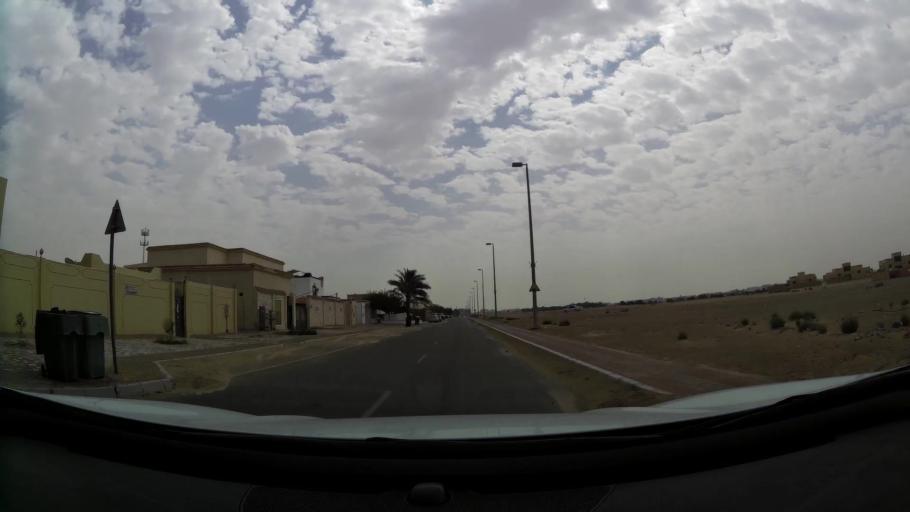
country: AE
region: Abu Dhabi
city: Abu Dhabi
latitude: 24.3131
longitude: 54.6278
